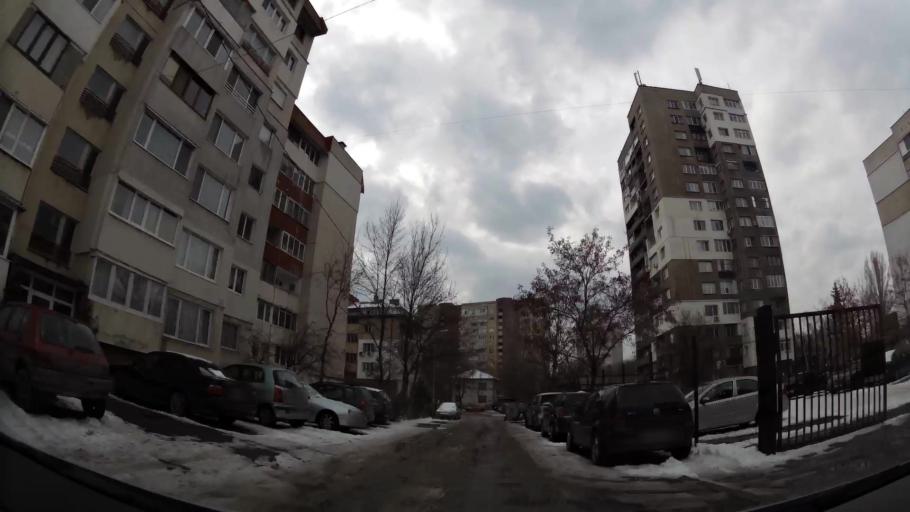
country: BG
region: Sofia-Capital
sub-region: Stolichna Obshtina
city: Sofia
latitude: 42.7035
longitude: 23.3663
